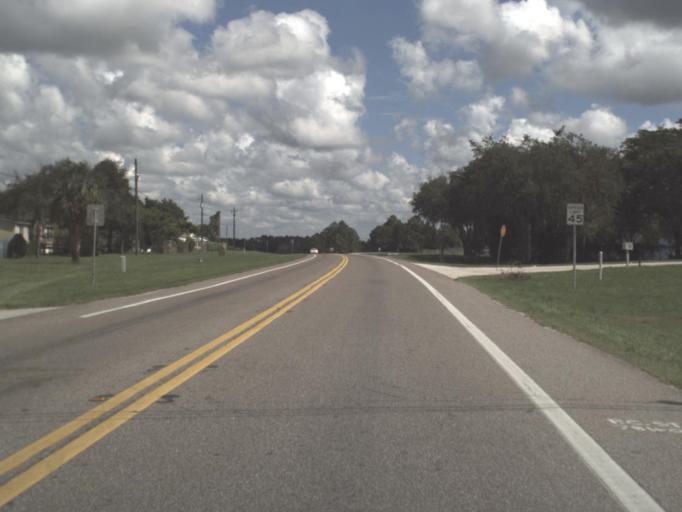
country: US
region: Florida
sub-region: Polk County
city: Polk City
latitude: 28.1856
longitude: -81.8222
